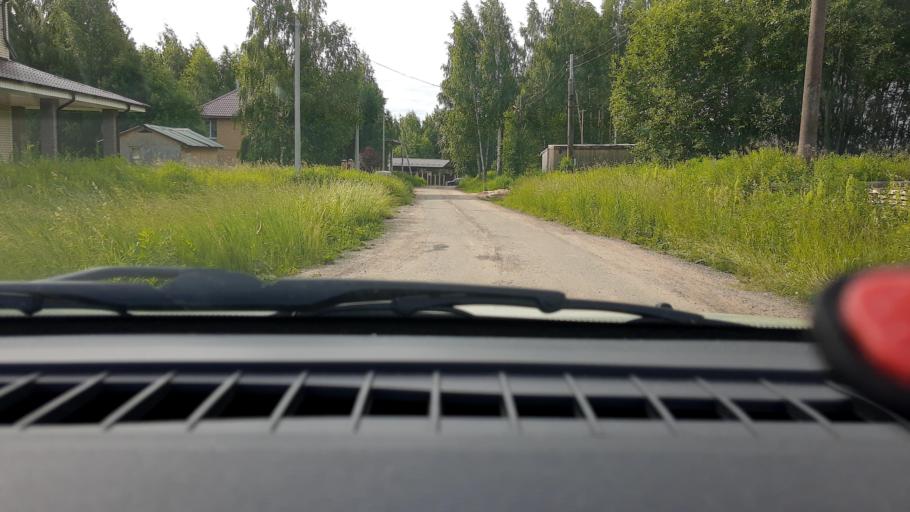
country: RU
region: Nizjnij Novgorod
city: Afonino
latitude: 56.2481
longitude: 44.0705
